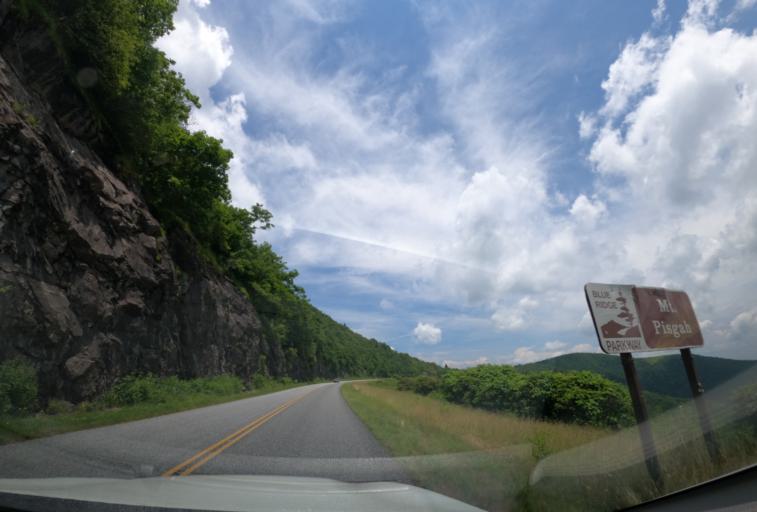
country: US
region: North Carolina
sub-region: Haywood County
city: Canton
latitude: 35.3988
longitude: -82.7603
